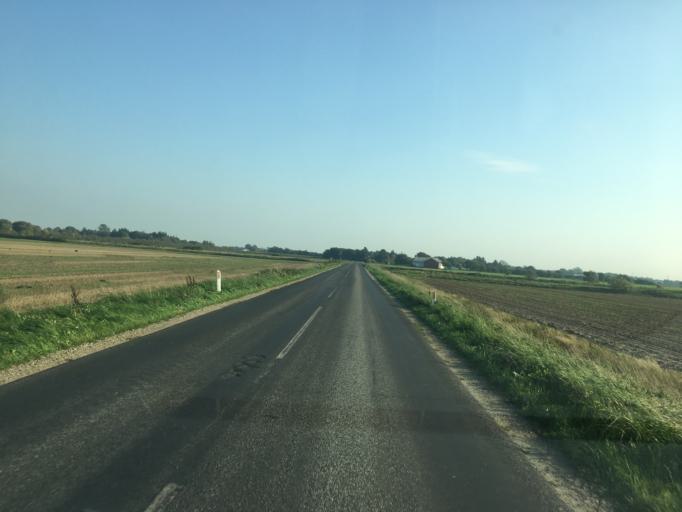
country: DE
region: Schleswig-Holstein
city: Bramstedtlund
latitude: 54.9440
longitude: 9.0630
